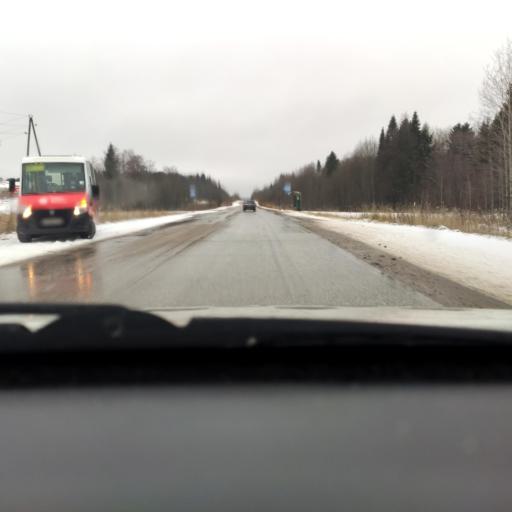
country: RU
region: Perm
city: Ferma
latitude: 57.9907
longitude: 56.3748
